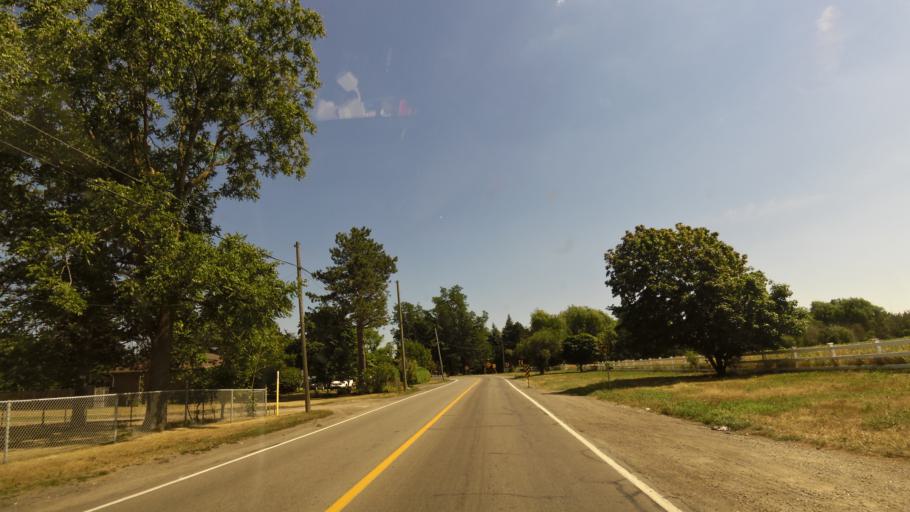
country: CA
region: Ontario
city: Brampton
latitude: 43.6420
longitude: -79.8566
